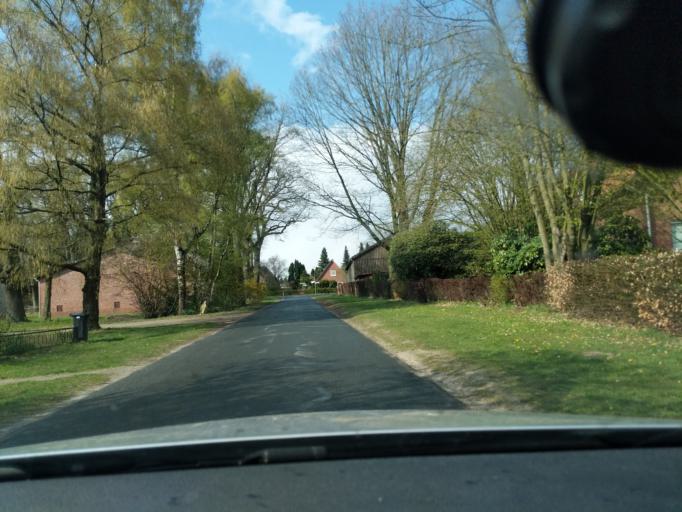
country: DE
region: Lower Saxony
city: Harsefeld
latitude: 53.4867
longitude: 9.5140
